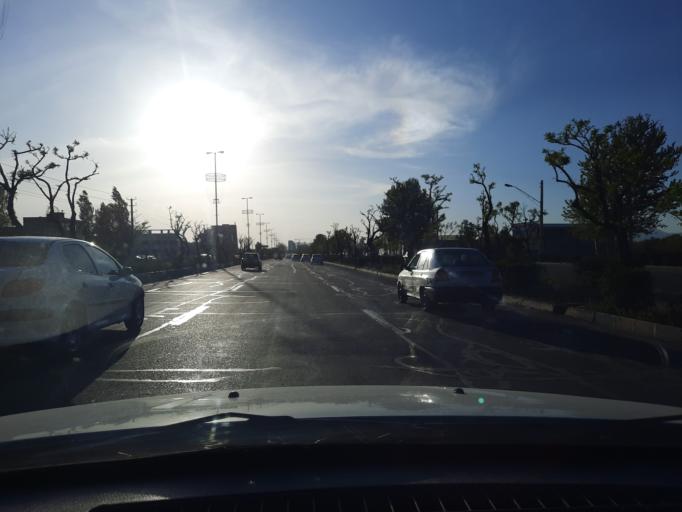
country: IR
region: Qazvin
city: Qazvin
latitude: 36.2634
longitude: 50.0386
